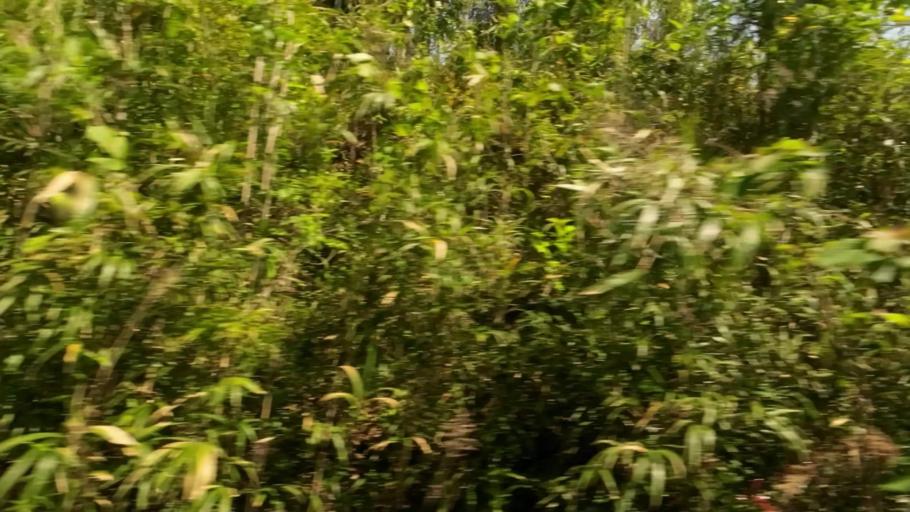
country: JP
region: Ehime
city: Niihama
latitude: 33.9723
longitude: 133.3517
